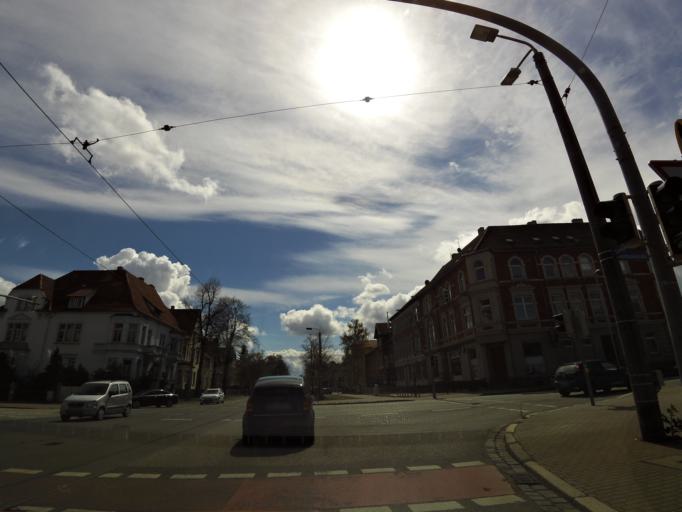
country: DE
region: Saxony-Anhalt
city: Halberstadt
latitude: 51.8893
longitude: 11.0490
